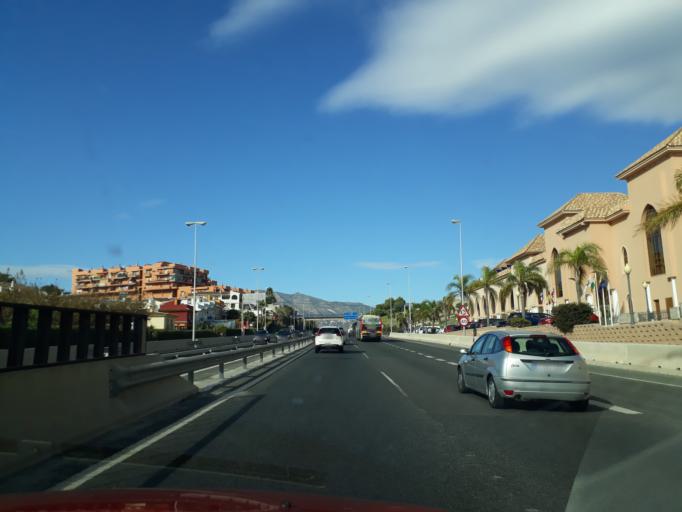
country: ES
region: Andalusia
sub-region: Provincia de Malaga
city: Fuengirola
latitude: 36.5212
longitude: -4.6301
